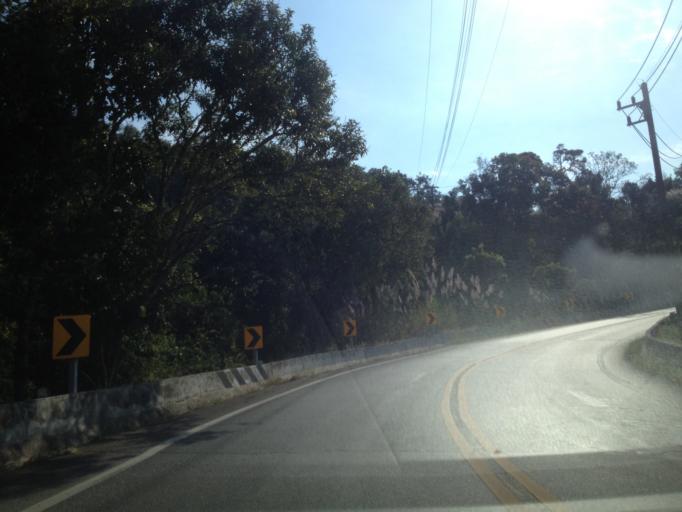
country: TH
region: Mae Hong Son
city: Ban Huai I Huak
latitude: 18.1486
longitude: 98.2632
